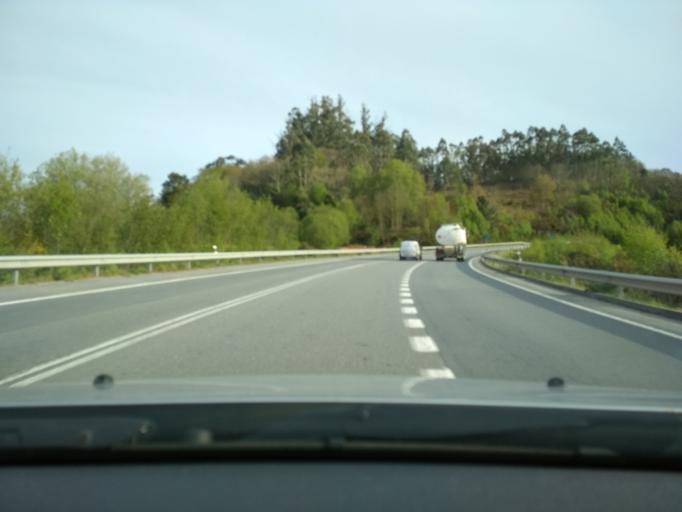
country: ES
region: Galicia
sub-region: Provincia da Coruna
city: Cerceda
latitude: 43.2168
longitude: -8.4556
